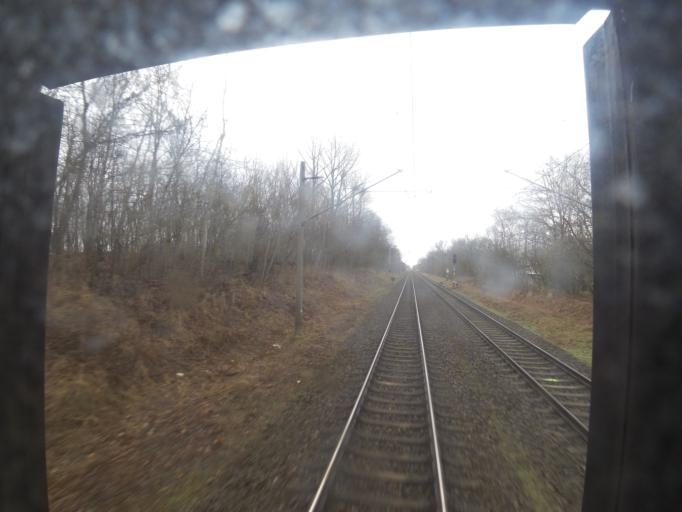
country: DE
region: Brandenburg
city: Rangsdorf
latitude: 52.3311
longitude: 13.4183
